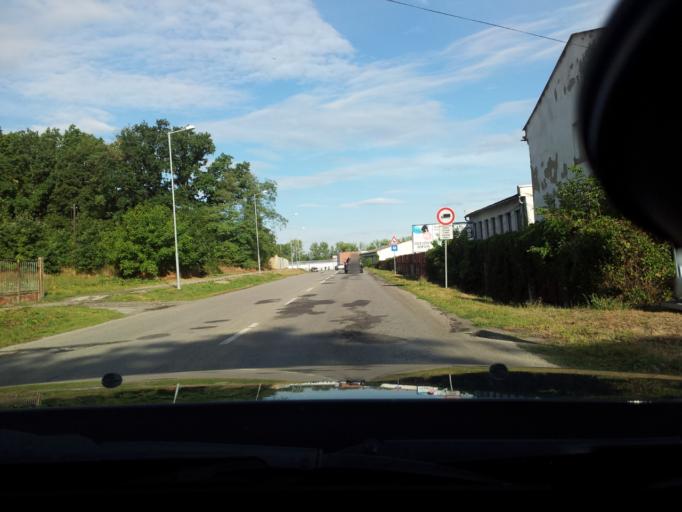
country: SK
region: Kosicky
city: Michalovce
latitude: 48.7664
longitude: 21.9029
